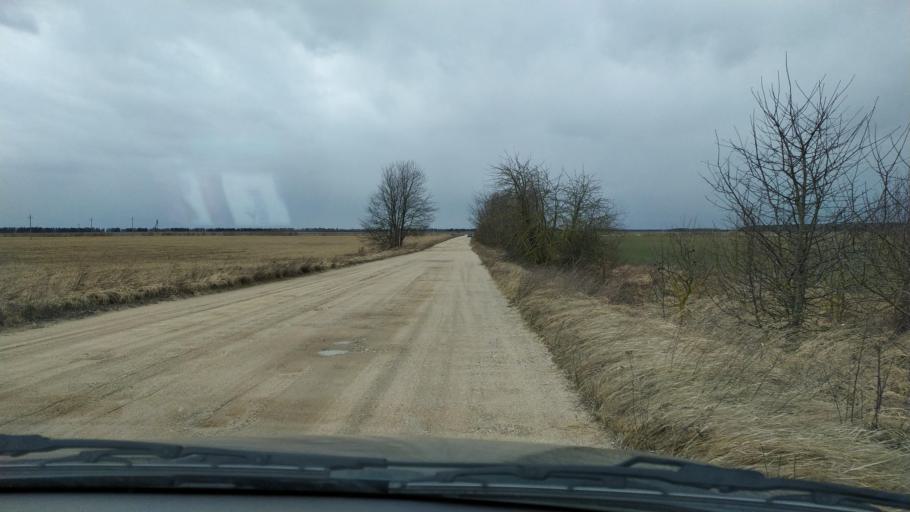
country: BY
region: Brest
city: Kamyanyets
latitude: 52.4256
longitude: 23.8201
